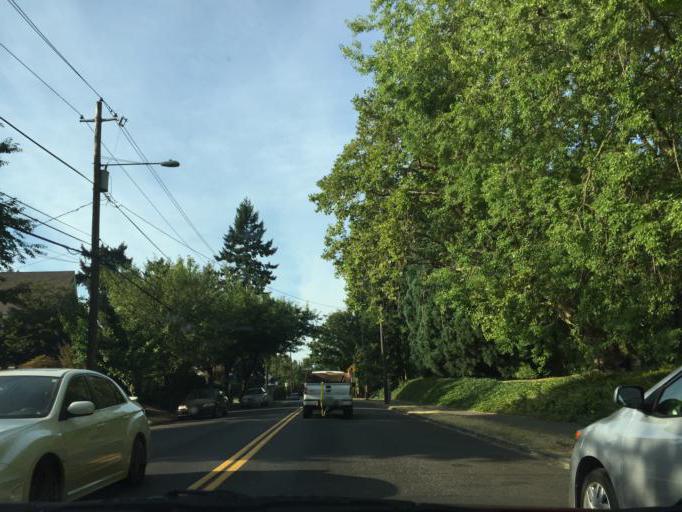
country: US
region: Oregon
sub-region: Multnomah County
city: Portland
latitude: 45.5394
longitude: -122.6307
